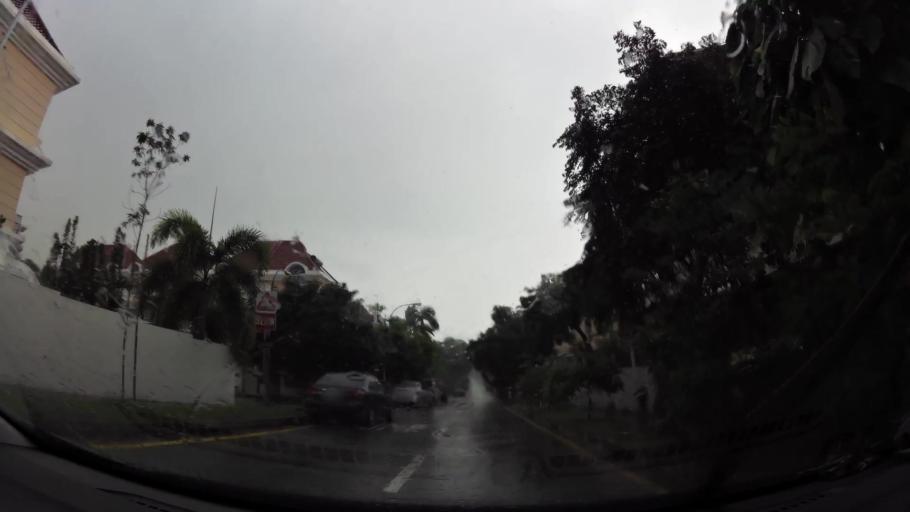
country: SG
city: Singapore
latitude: 1.3397
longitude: 103.9550
